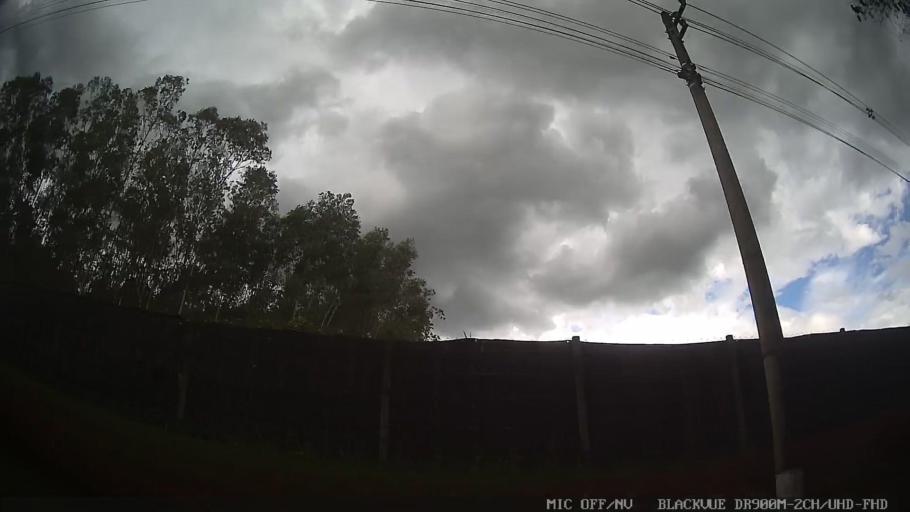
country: BR
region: Sao Paulo
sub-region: Jaguariuna
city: Jaguariuna
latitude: -22.6391
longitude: -47.0603
